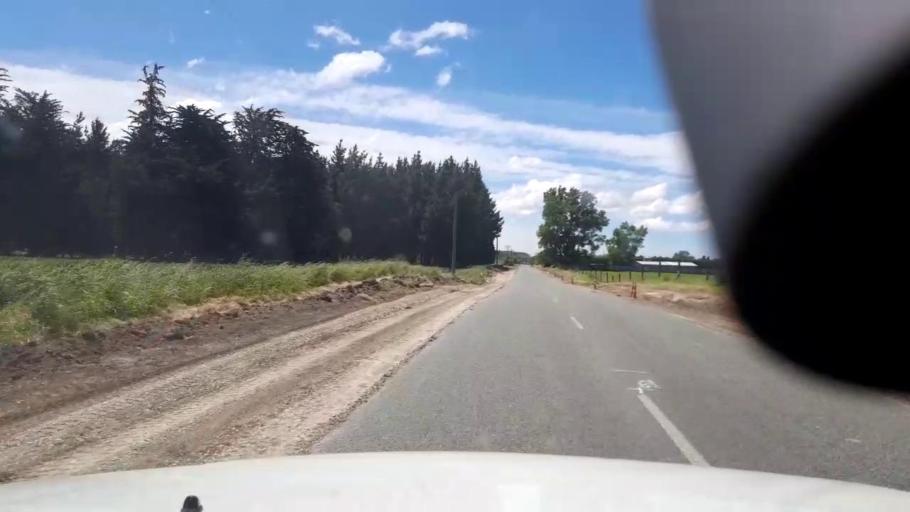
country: NZ
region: Canterbury
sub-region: Timaru District
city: Pleasant Point
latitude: -44.2766
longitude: 171.2505
